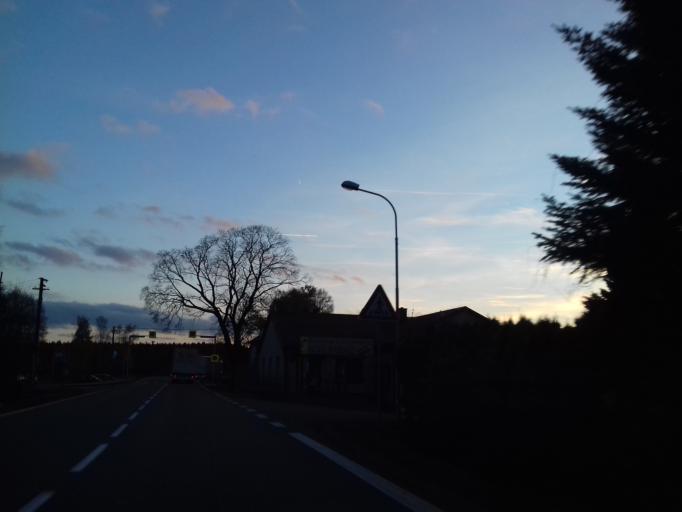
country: CZ
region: Vysocina
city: Krizova
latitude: 49.6919
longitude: 15.7969
